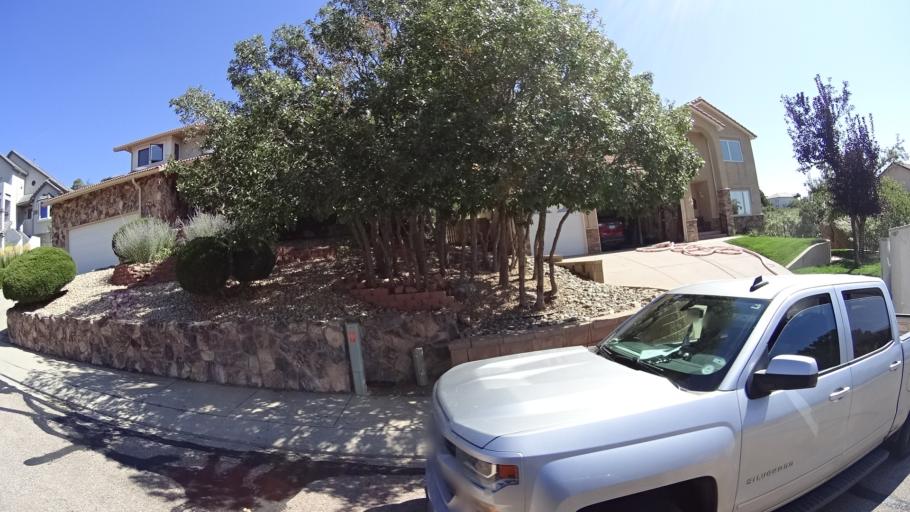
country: US
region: Colorado
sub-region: El Paso County
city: Cimarron Hills
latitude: 38.9132
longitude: -104.7508
